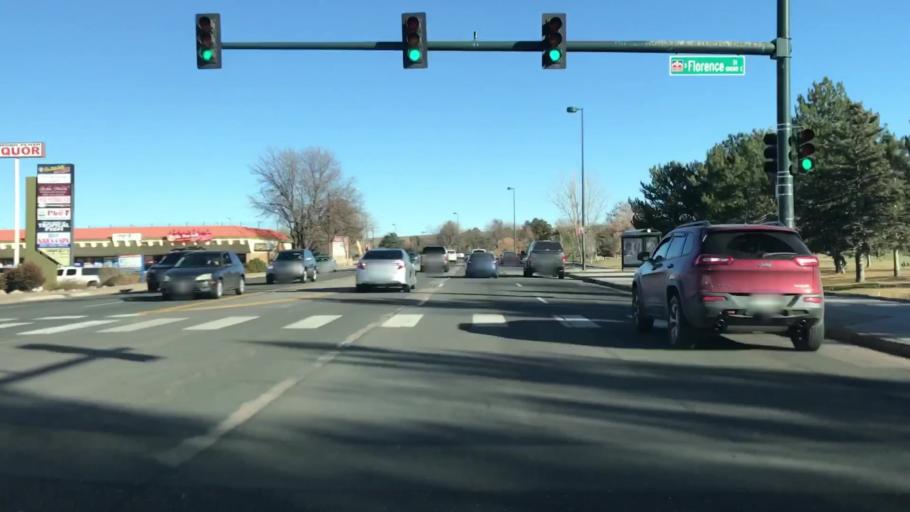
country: US
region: Colorado
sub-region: Arapahoe County
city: Centennial
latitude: 39.6530
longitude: -104.8720
